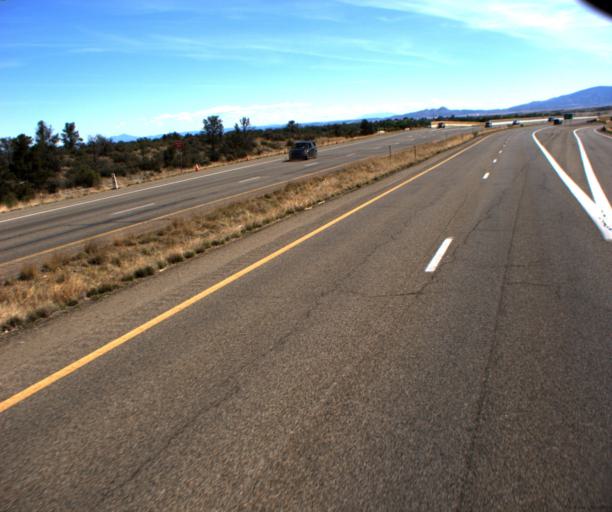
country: US
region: Arizona
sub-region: Yavapai County
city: Prescott
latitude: 34.6304
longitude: -112.4341
